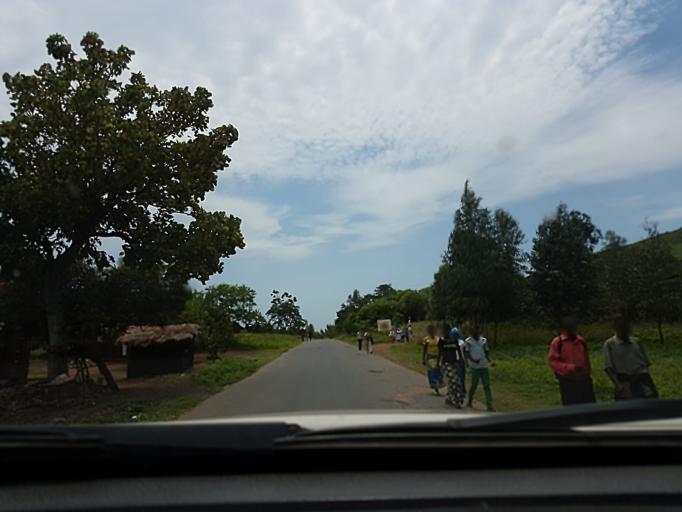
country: CD
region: South Kivu
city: Uvira
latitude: -3.2484
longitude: 29.1612
